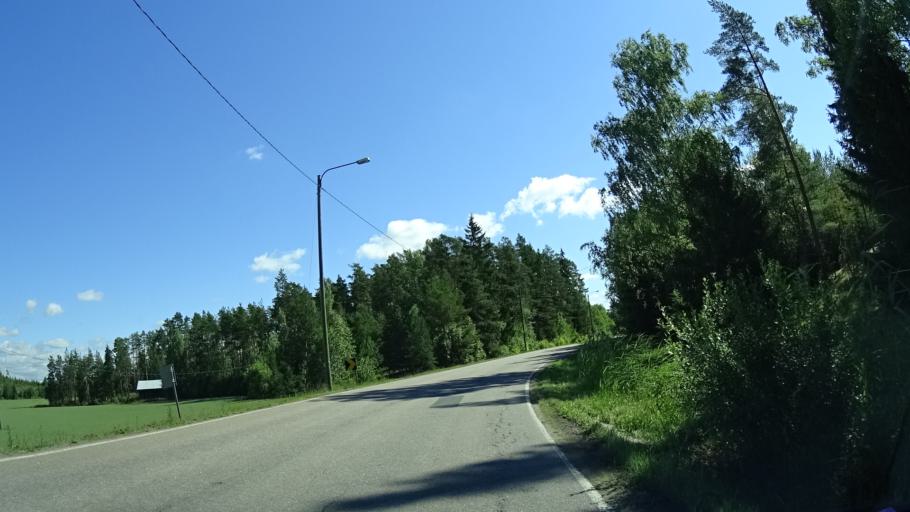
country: FI
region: Varsinais-Suomi
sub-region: Turku
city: Askainen
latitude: 60.5707
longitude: 21.8983
